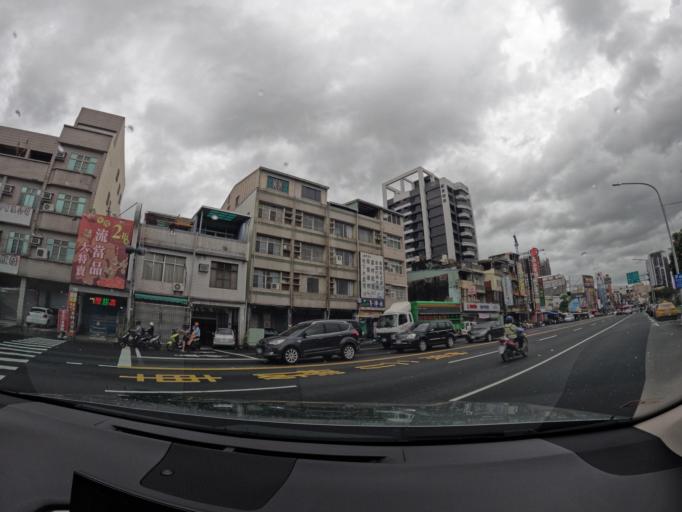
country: TW
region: Taiwan
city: Fengshan
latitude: 22.6221
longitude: 120.3671
